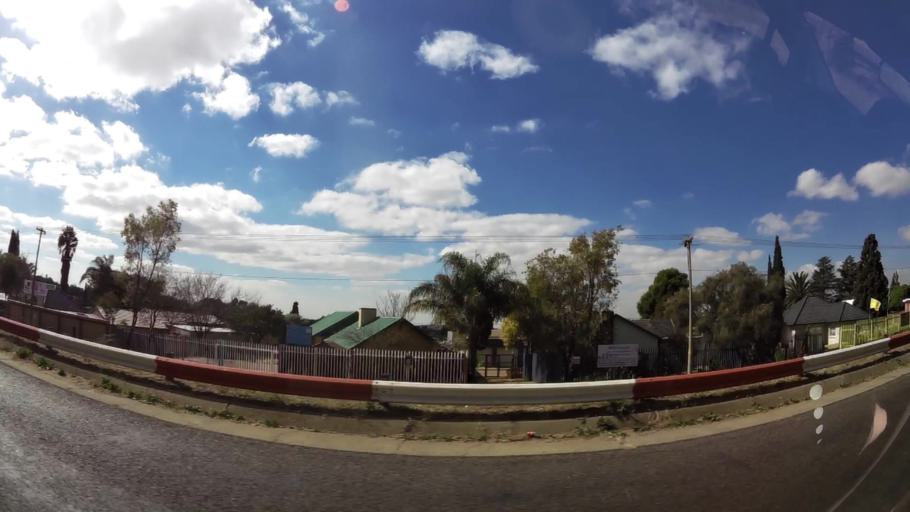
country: ZA
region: Gauteng
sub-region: West Rand District Municipality
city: Krugersdorp
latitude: -26.1164
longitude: 27.8168
